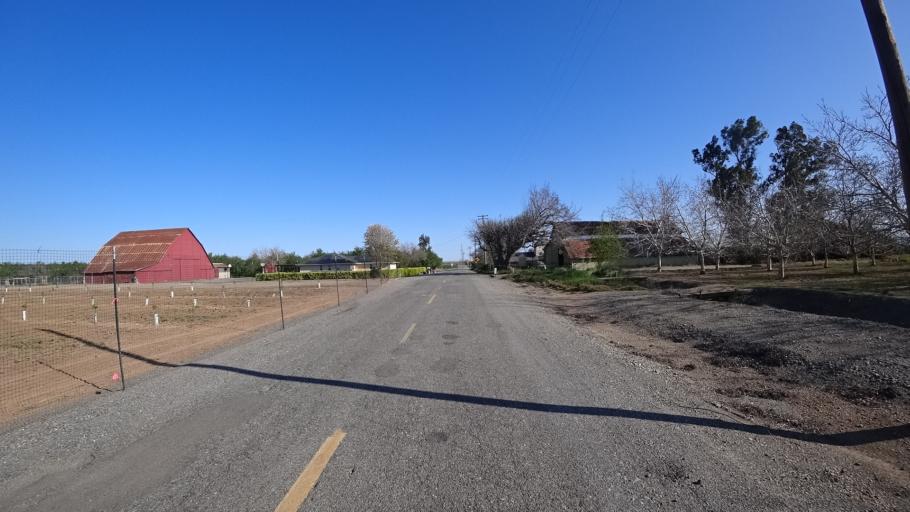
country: US
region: California
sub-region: Glenn County
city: Orland
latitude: 39.7664
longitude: -122.1322
